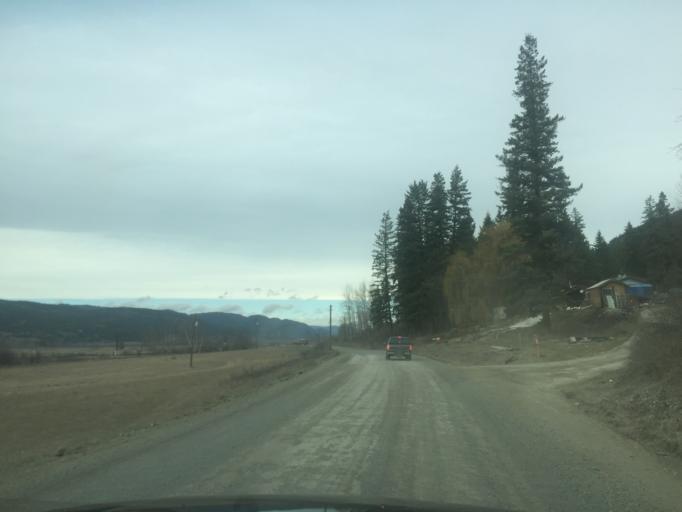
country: CA
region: British Columbia
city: Kamloops
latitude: 51.2458
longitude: -120.1477
